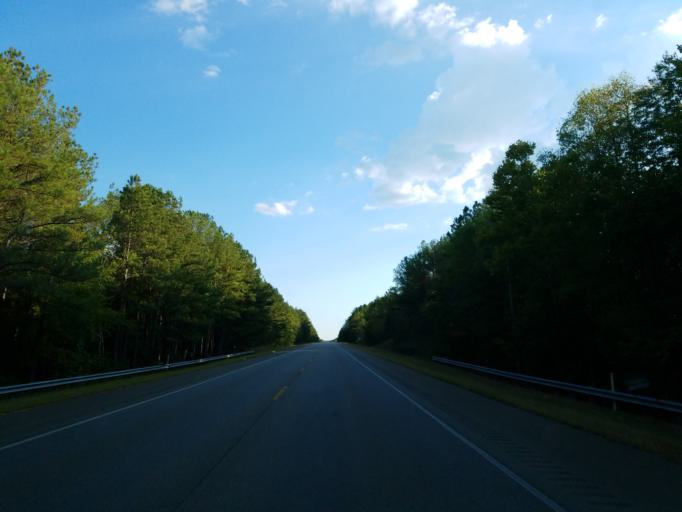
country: US
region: Georgia
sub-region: Murray County
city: Chatsworth
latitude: 34.6346
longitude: -84.7138
